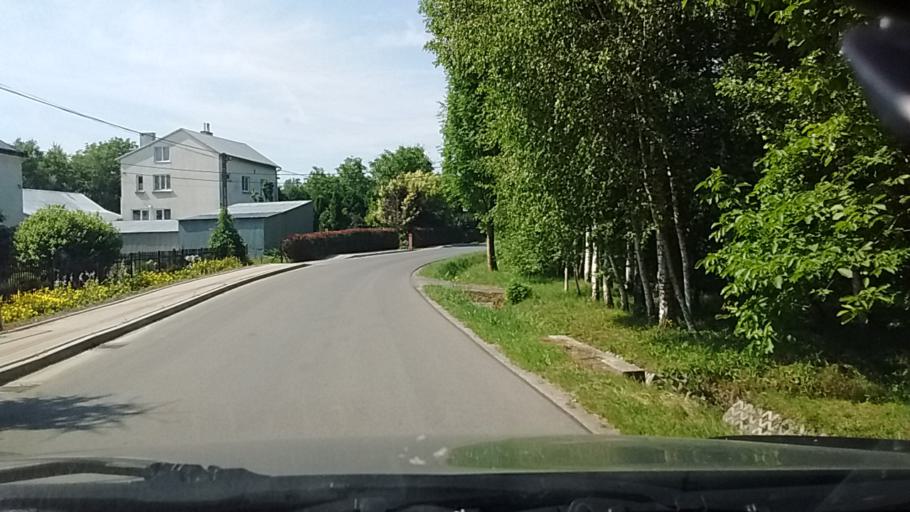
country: PL
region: Subcarpathian Voivodeship
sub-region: Powiat lancucki
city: Wysoka
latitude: 50.0480
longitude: 22.2539
